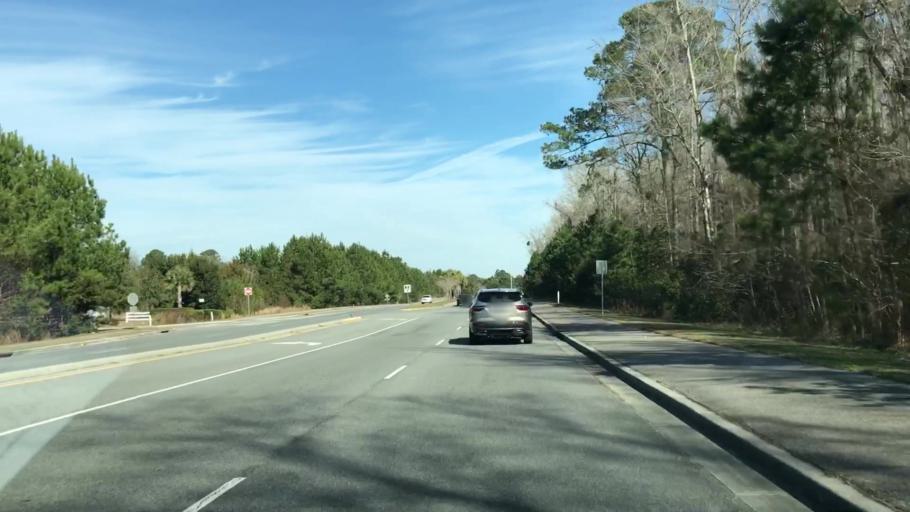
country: US
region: South Carolina
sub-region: Beaufort County
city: Bluffton
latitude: 32.2623
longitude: -80.8866
